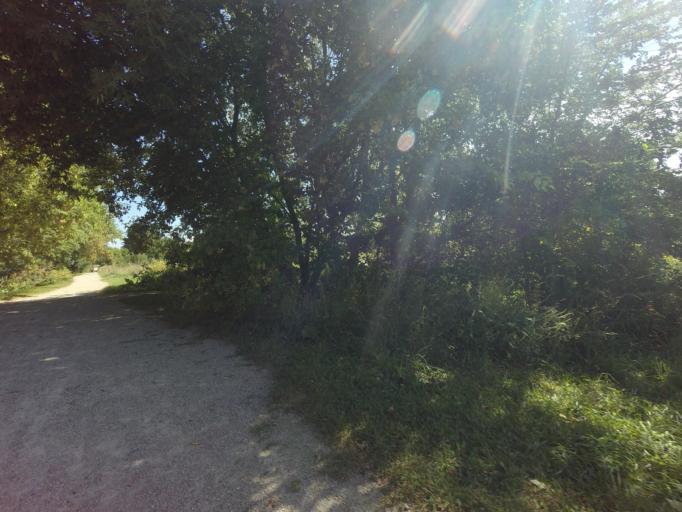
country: CA
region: Ontario
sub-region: Wellington County
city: Guelph
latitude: 43.6896
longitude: -80.4197
